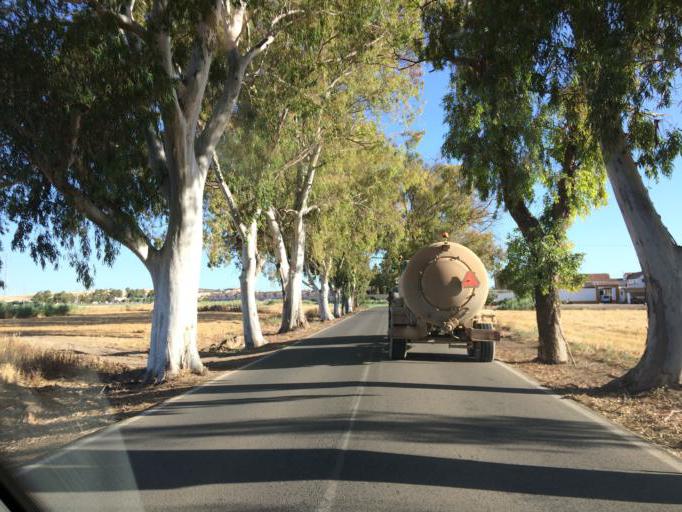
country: ES
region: Andalusia
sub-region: Provincia de Malaga
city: Campillos
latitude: 37.0367
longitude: -4.8577
